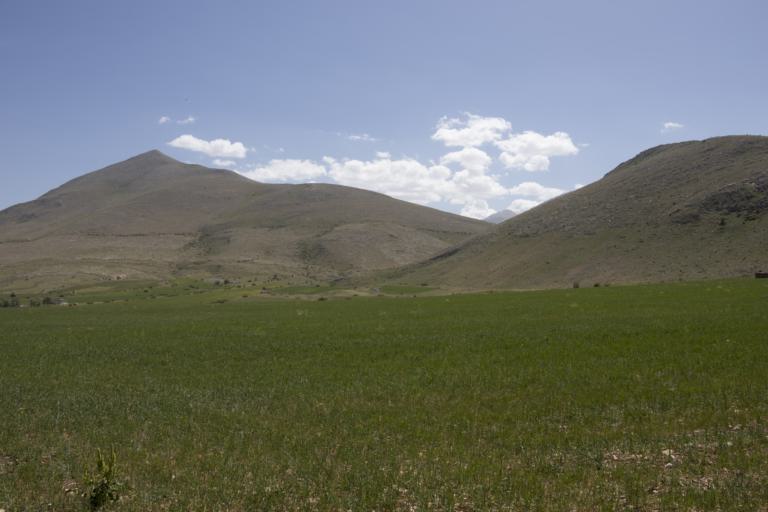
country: TR
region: Kayseri
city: Toklar
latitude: 38.4175
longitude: 36.0955
